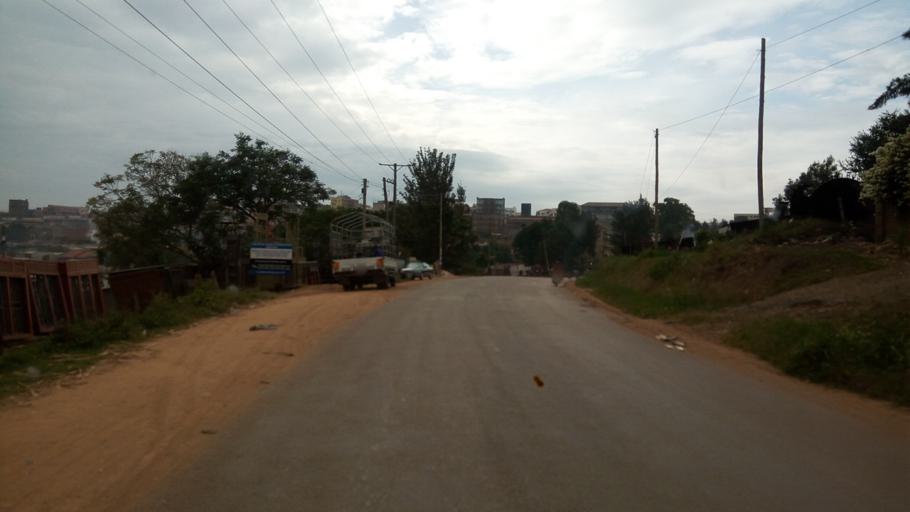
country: UG
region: Western Region
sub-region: Mbarara District
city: Mbarara
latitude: -0.6051
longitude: 30.6569
